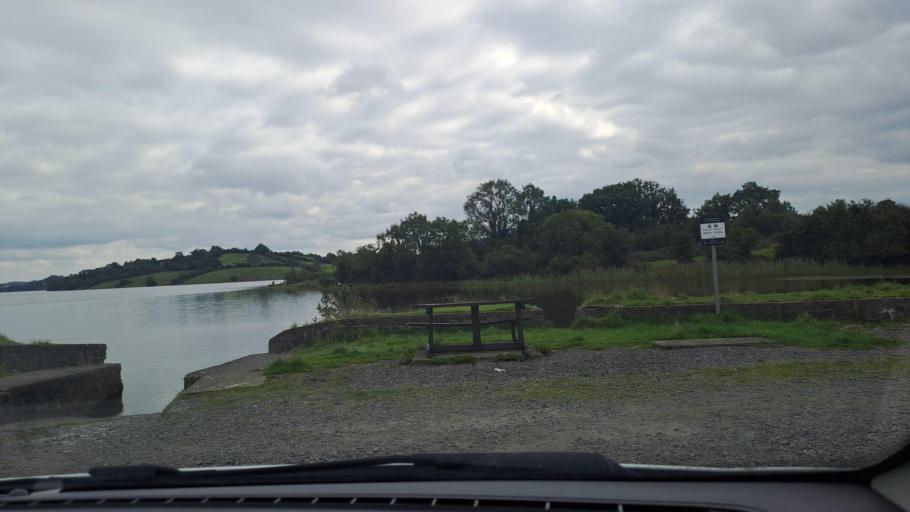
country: IE
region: Ulster
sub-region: An Cabhan
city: Bailieborough
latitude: 54.0108
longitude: -6.9448
